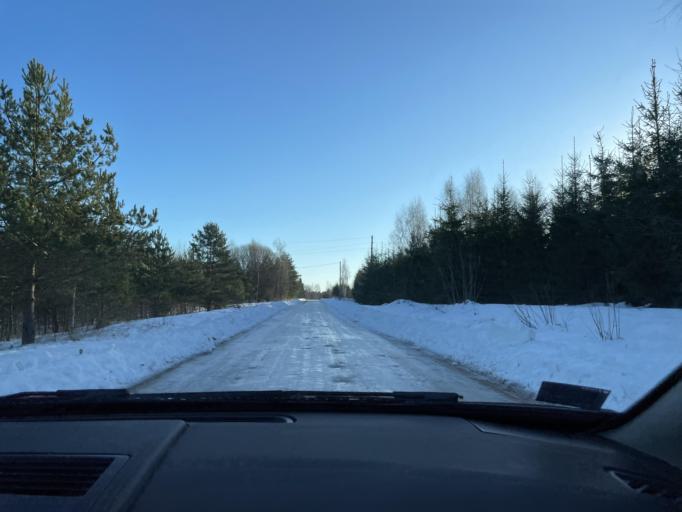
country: LV
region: Ludzas Rajons
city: Ludza
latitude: 56.4637
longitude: 27.6054
